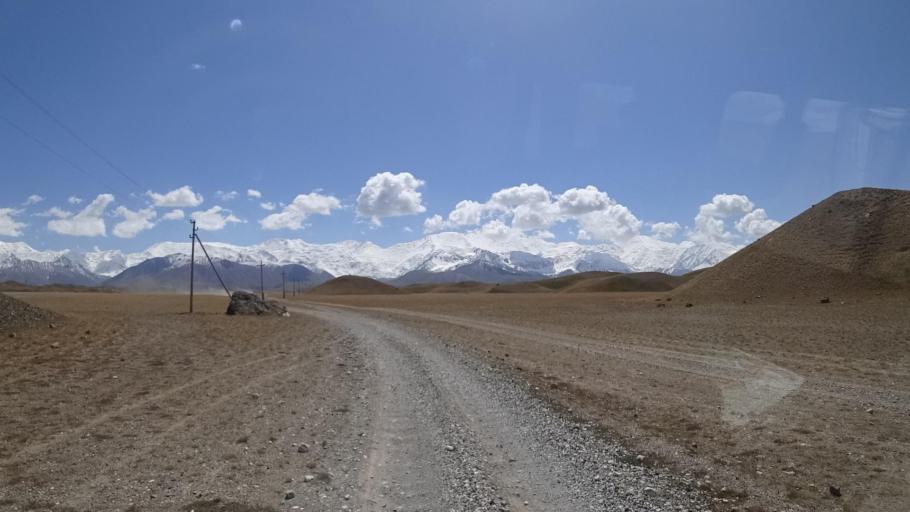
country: KG
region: Osh
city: Gul'cha
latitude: 39.5896
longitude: 72.8869
